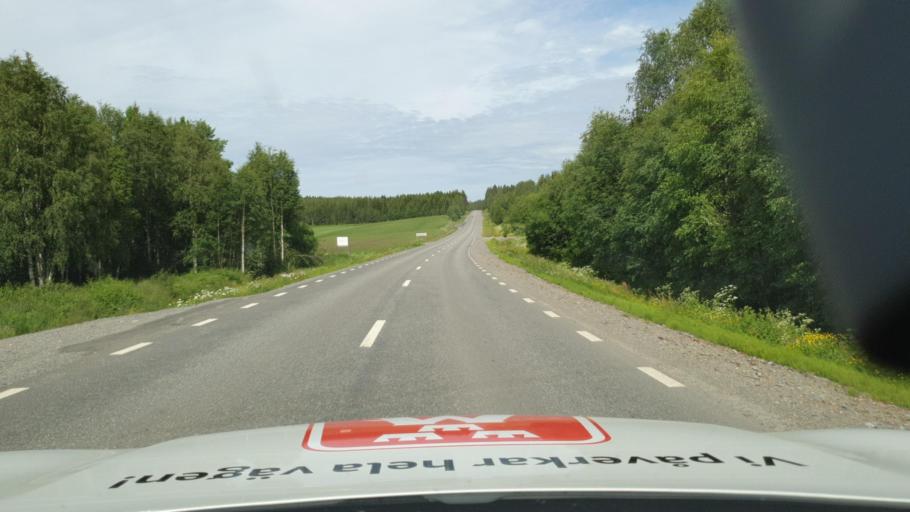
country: SE
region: Vaesterbotten
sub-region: Skelleftea Kommun
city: Burtraesk
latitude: 64.3666
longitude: 20.5011
